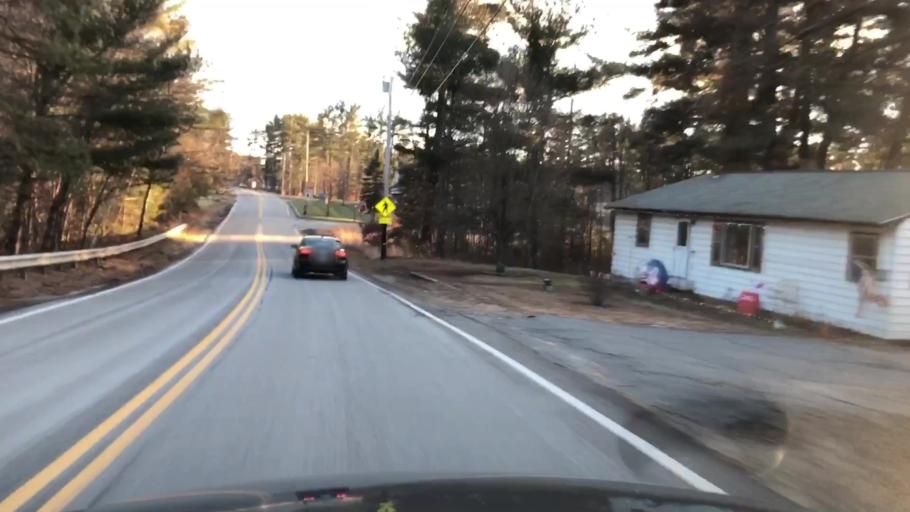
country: US
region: Massachusetts
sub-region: Middlesex County
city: Townsend
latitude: 42.6778
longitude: -71.6998
